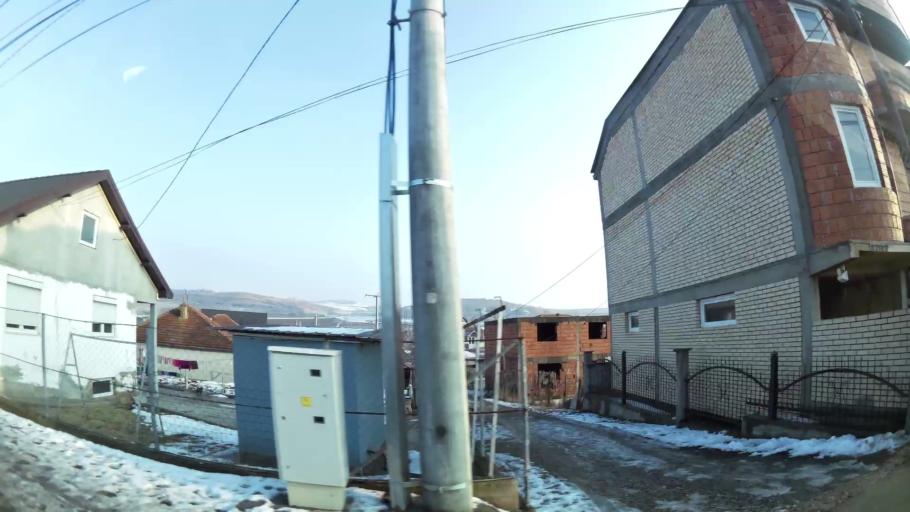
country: MK
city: Miladinovci
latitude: 41.9901
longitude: 21.6529
